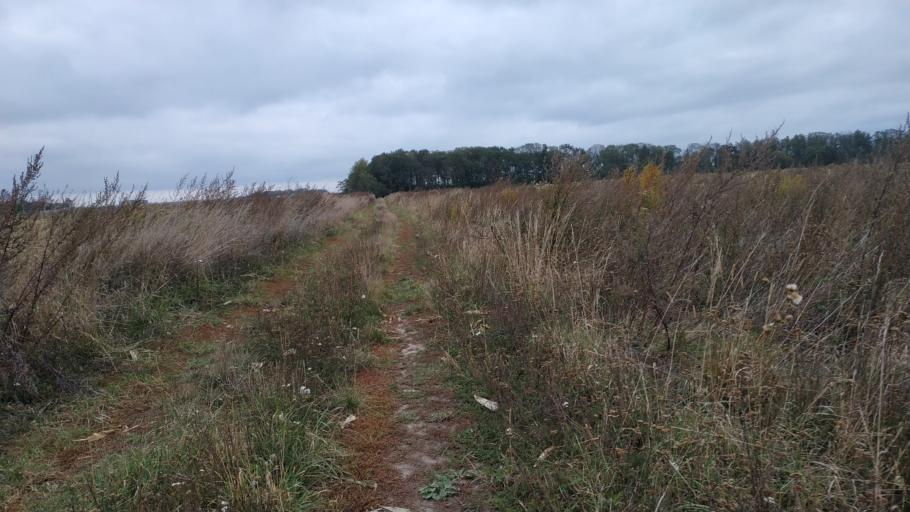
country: PL
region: Lower Silesian Voivodeship
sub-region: Powiat wroclawski
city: Tyniec Maly
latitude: 51.0256
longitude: 16.9435
